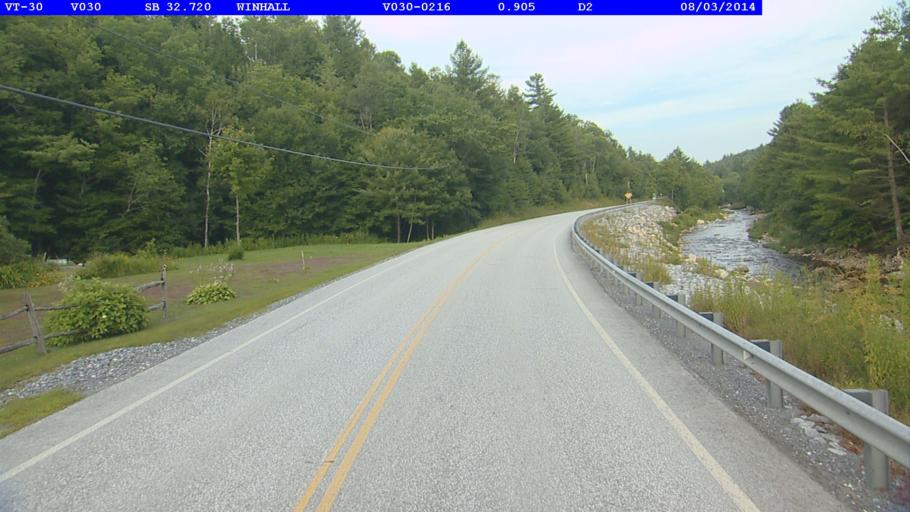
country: US
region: Vermont
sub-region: Bennington County
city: Manchester Center
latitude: 43.1448
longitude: -72.8842
